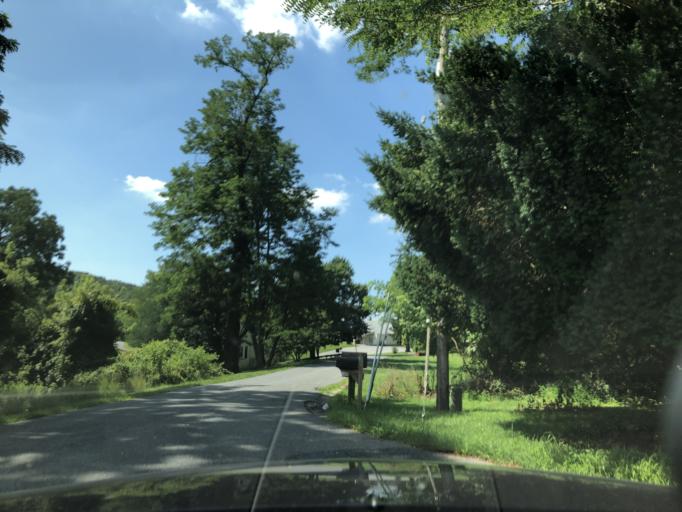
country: US
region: Maryland
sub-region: Carroll County
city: Westminster
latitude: 39.5934
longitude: -76.9688
